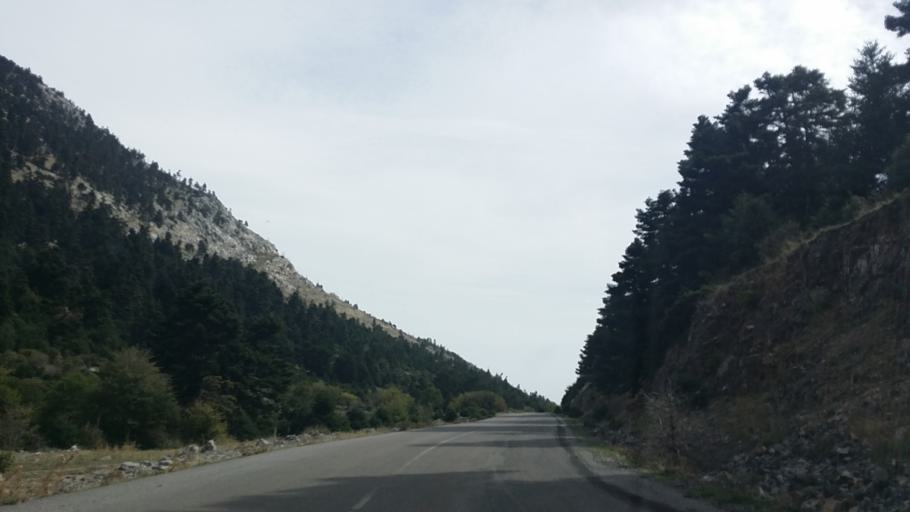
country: GR
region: Central Greece
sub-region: Nomos Voiotias
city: Kyriaki
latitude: 38.3332
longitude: 22.8371
